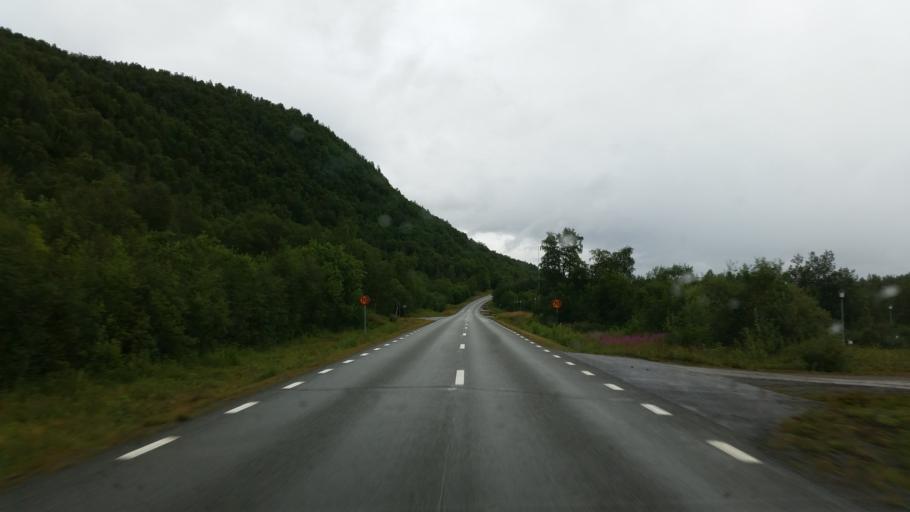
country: NO
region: Nordland
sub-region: Rana
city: Mo i Rana
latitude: 65.8770
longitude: 15.0019
